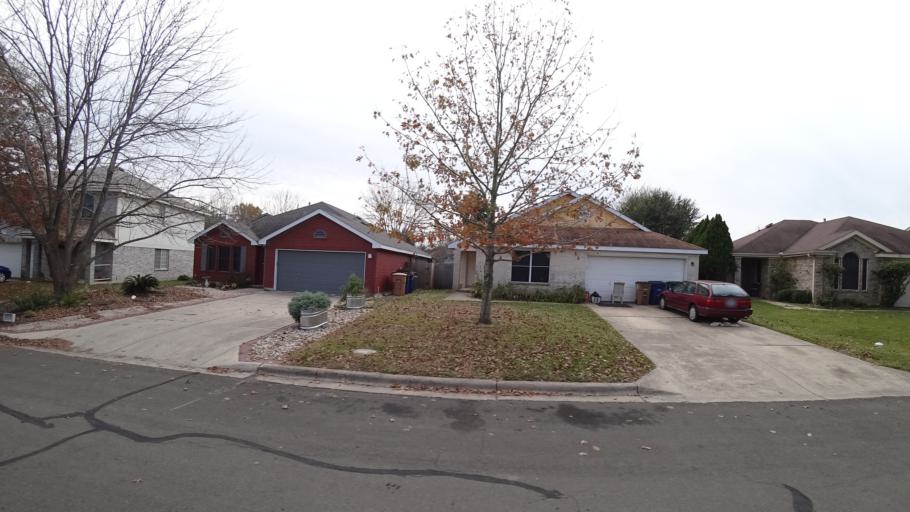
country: US
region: Texas
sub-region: Travis County
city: Onion Creek
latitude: 30.1583
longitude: -97.7370
